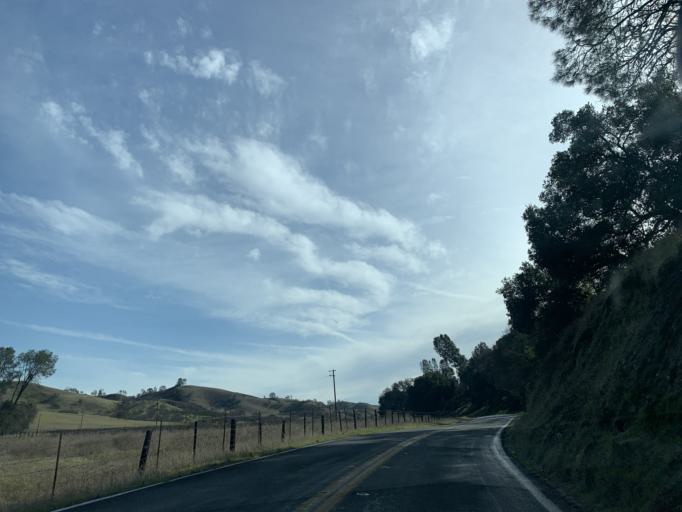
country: US
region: California
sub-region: Monterey County
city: Soledad
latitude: 36.5162
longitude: -121.1245
